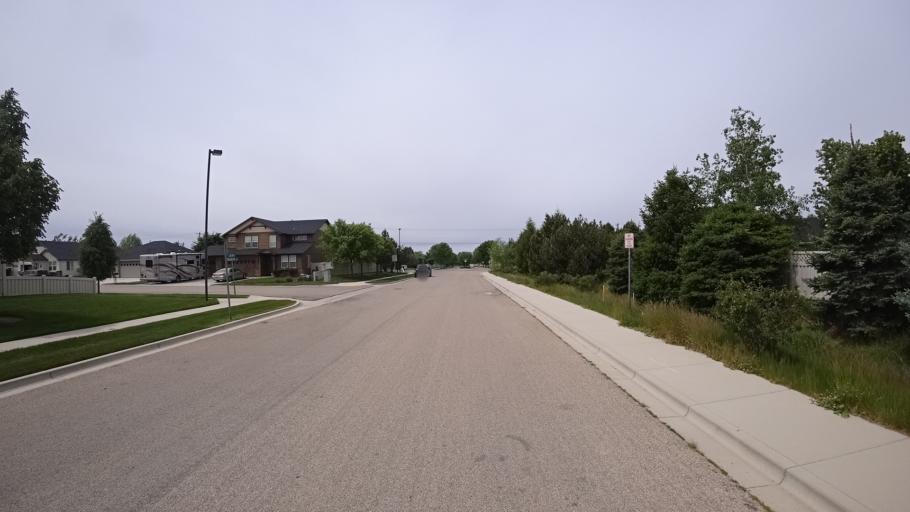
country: US
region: Idaho
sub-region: Ada County
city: Meridian
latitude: 43.5666
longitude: -116.3533
